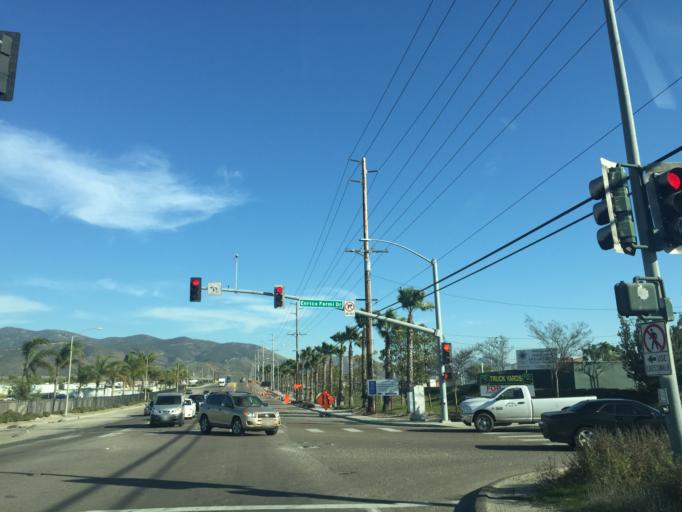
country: MX
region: Baja California
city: Tijuana
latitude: 32.5674
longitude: -116.9280
